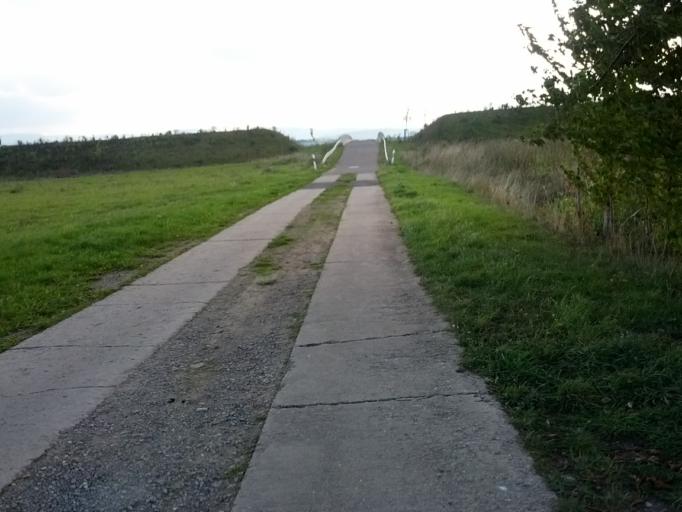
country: DE
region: Thuringia
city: Eisenach
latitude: 51.0158
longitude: 10.3379
